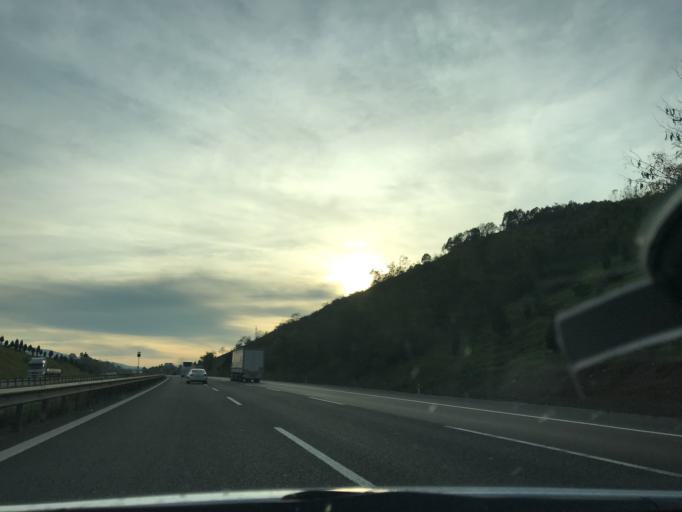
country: TR
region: Duzce
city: Gumusova
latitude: 40.8249
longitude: 30.9211
